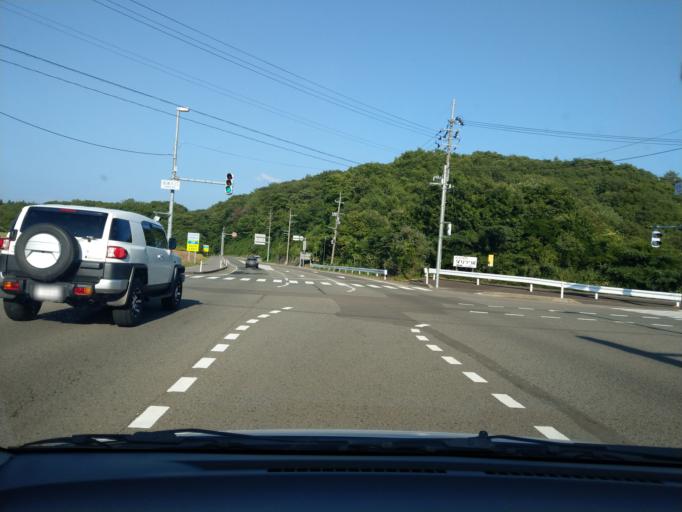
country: JP
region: Akita
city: Akita
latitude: 39.6090
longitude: 140.2019
